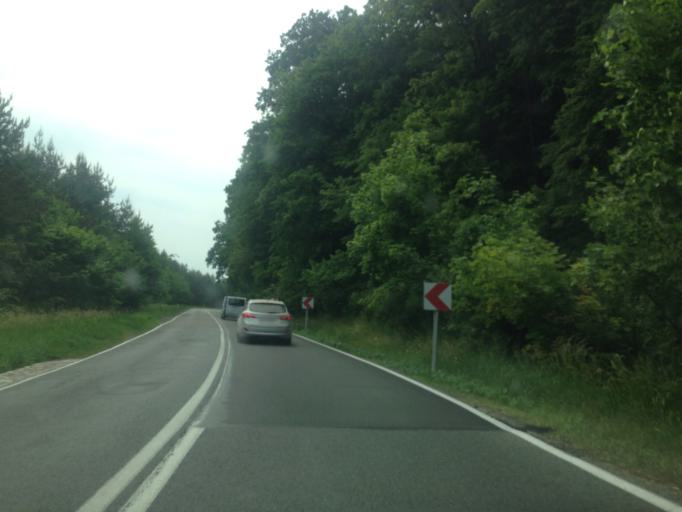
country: PL
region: Kujawsko-Pomorskie
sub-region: Powiat grudziadzki
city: Rogozno
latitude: 53.5045
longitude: 18.9055
